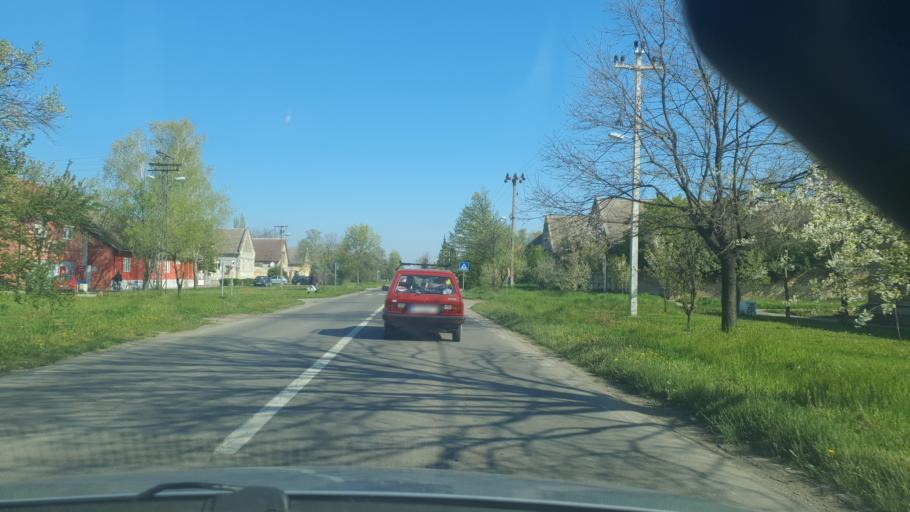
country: RS
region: Autonomna Pokrajina Vojvodina
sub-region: Zapadnobacki Okrug
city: Kula
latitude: 45.7076
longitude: 19.3807
